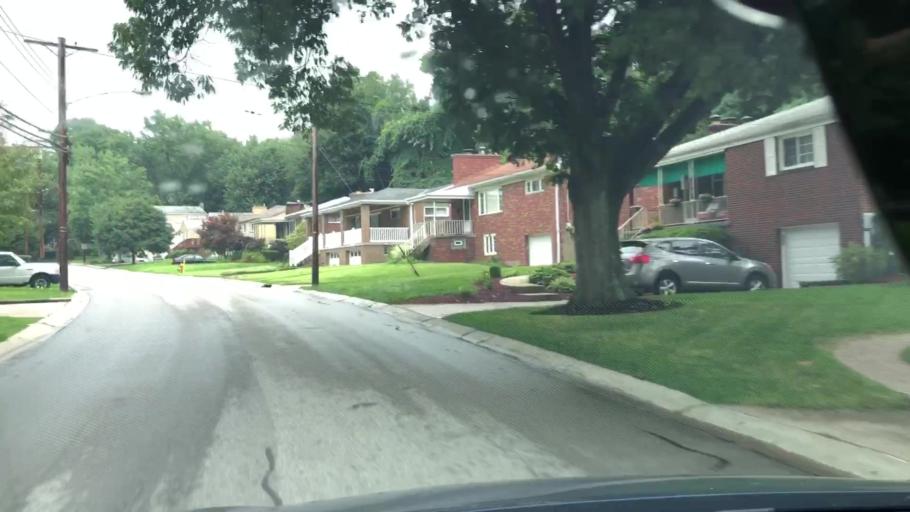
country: US
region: Pennsylvania
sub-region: Allegheny County
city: Castle Shannon
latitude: 40.3776
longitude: -80.0247
